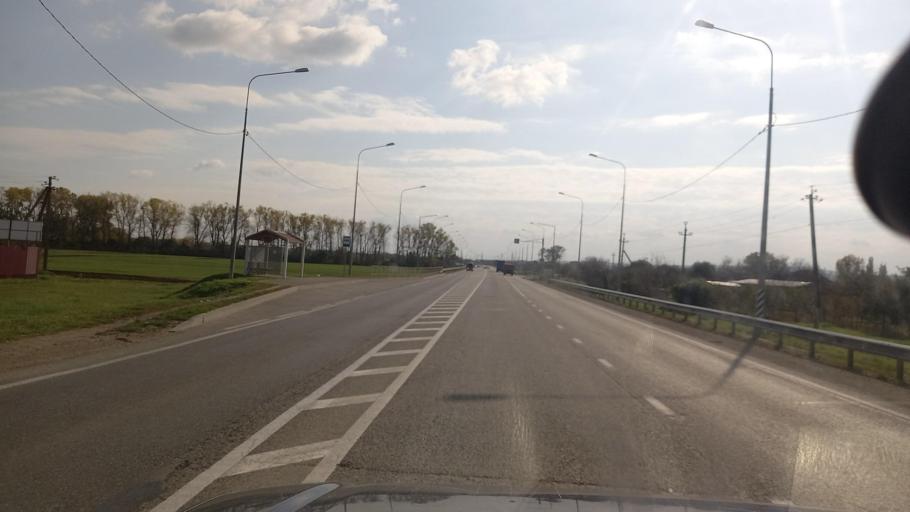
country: RU
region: Krasnodarskiy
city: Novoukrainskiy
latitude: 44.9031
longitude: 38.0334
